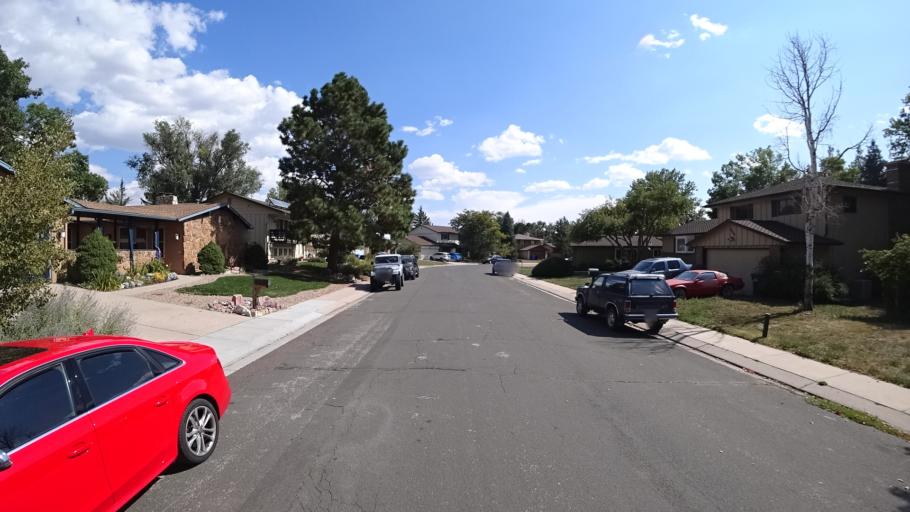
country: US
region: Colorado
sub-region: El Paso County
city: Cimarron Hills
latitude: 38.8747
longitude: -104.7510
